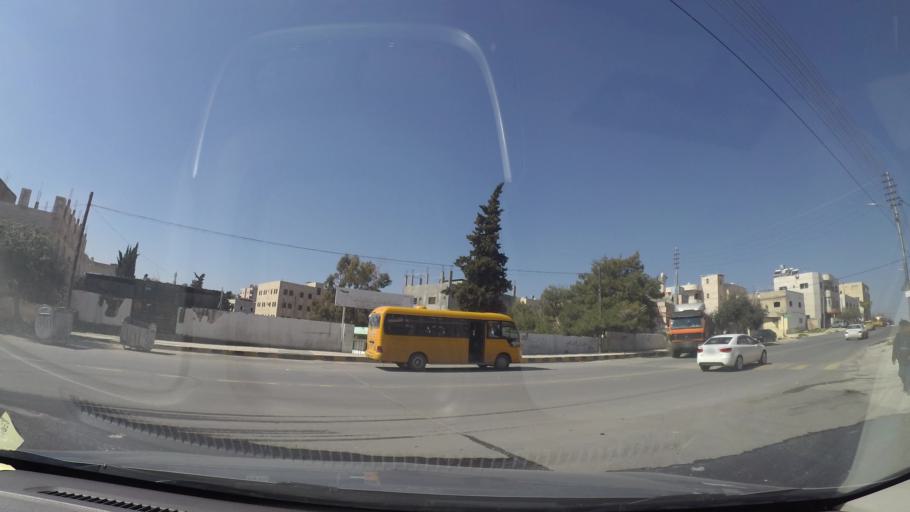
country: JO
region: Amman
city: Al Bunayyat ash Shamaliyah
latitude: 31.9062
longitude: 35.9032
